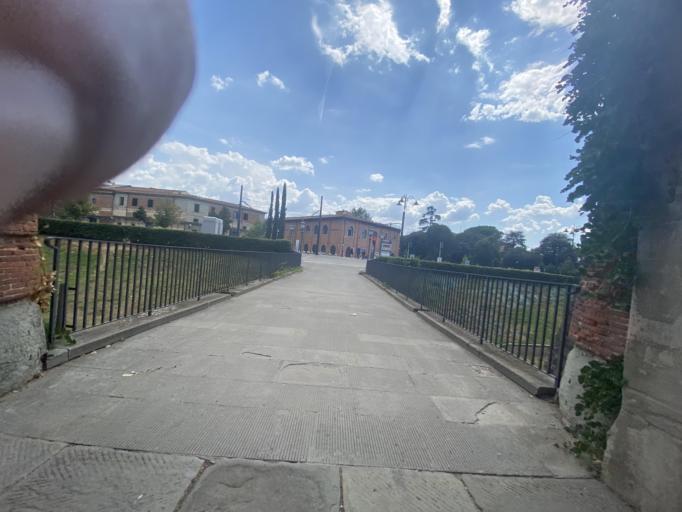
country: IT
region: Tuscany
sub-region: Province of Florence
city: Florence
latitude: 43.7810
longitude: 11.2497
